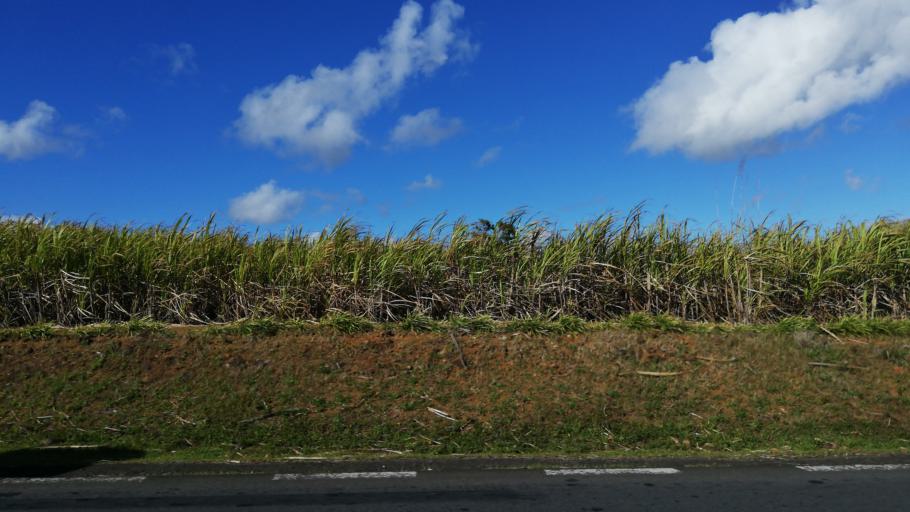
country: MU
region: Moka
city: La Dagotiere
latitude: -20.2324
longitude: 57.5612
